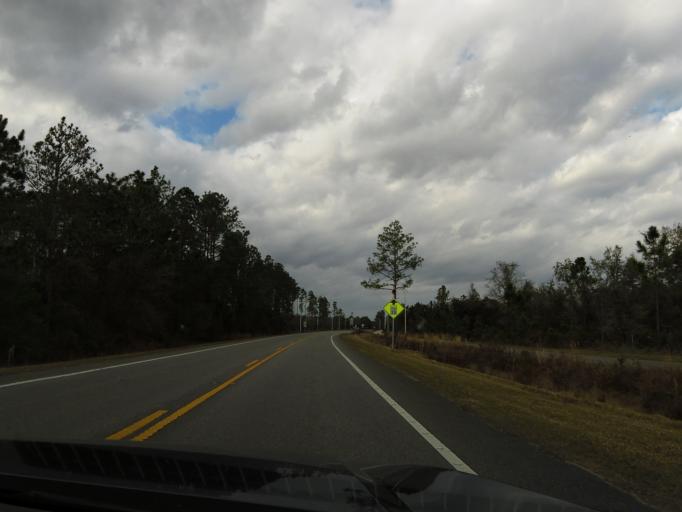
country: US
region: Florida
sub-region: Volusia County
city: Pierson
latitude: 29.2548
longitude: -81.4684
